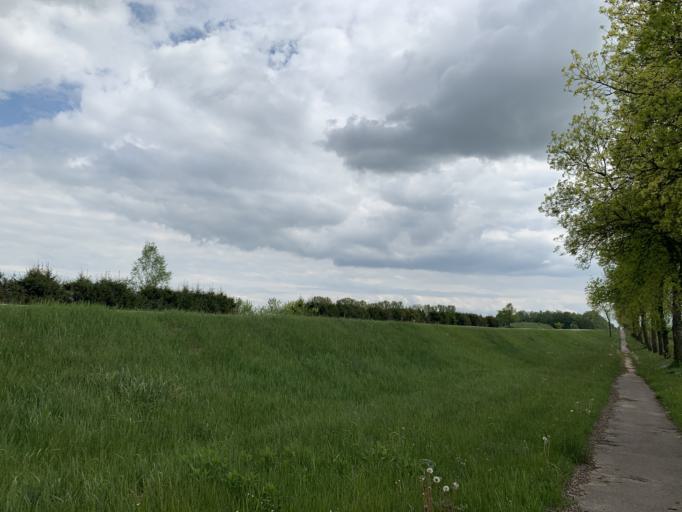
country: BY
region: Minsk
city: Nyasvizh
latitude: 53.2422
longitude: 26.6764
